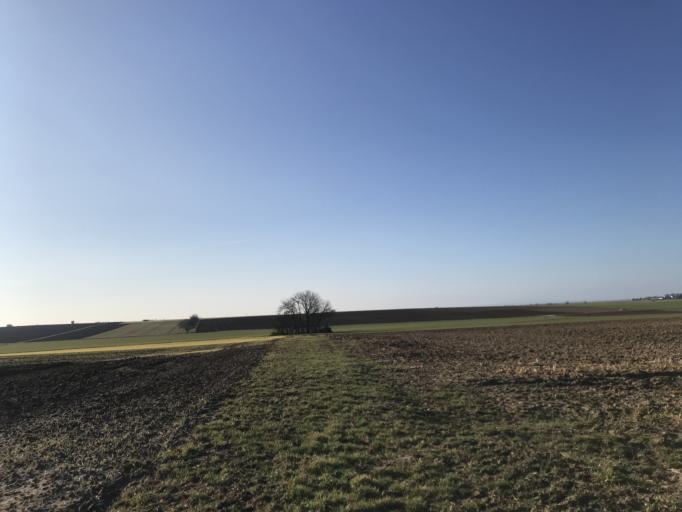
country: DE
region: Rheinland-Pfalz
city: Essenheim
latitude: 49.9488
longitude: 8.1477
